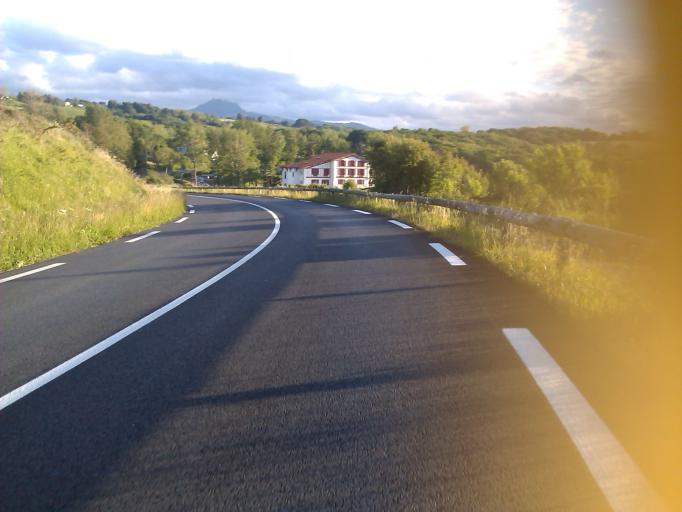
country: FR
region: Aquitaine
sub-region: Departement des Pyrenees-Atlantiques
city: Urrugne
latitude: 43.3815
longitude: -1.7321
